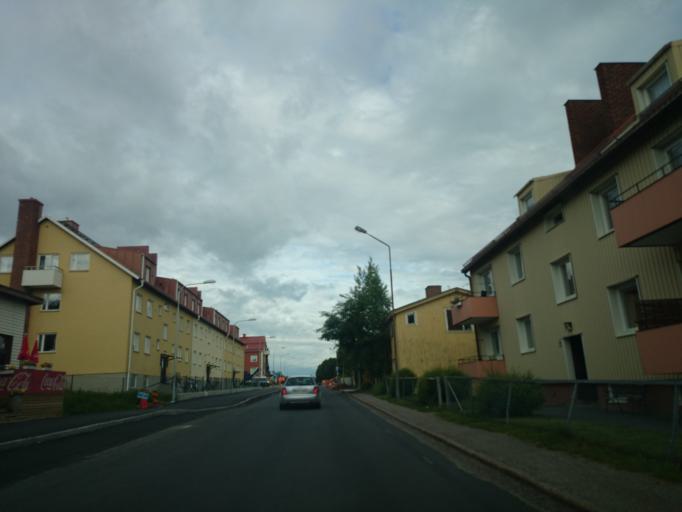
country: SE
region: Vaesternorrland
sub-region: Sundsvalls Kommun
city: Sundsvall
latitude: 62.3804
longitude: 17.3319
